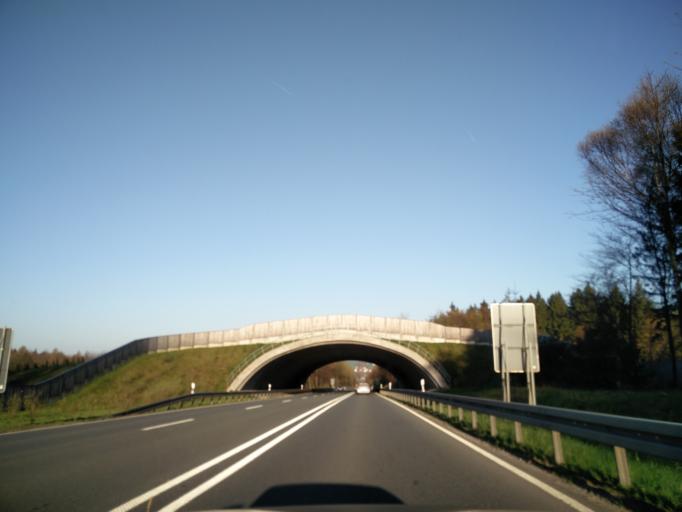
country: DE
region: North Rhine-Westphalia
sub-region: Regierungsbezirk Detmold
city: Altenbeken
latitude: 51.7396
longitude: 8.9765
